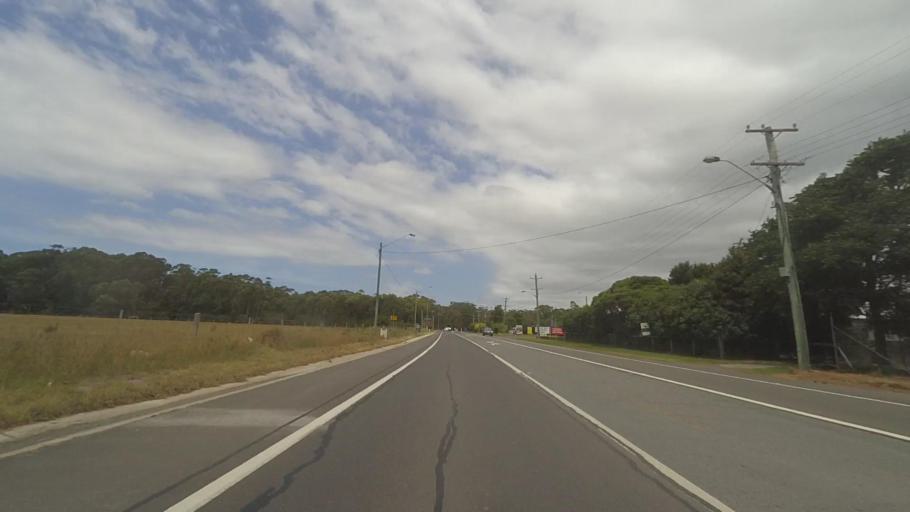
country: AU
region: New South Wales
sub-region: Shoalhaven Shire
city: Falls Creek
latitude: -35.0928
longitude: 150.5071
